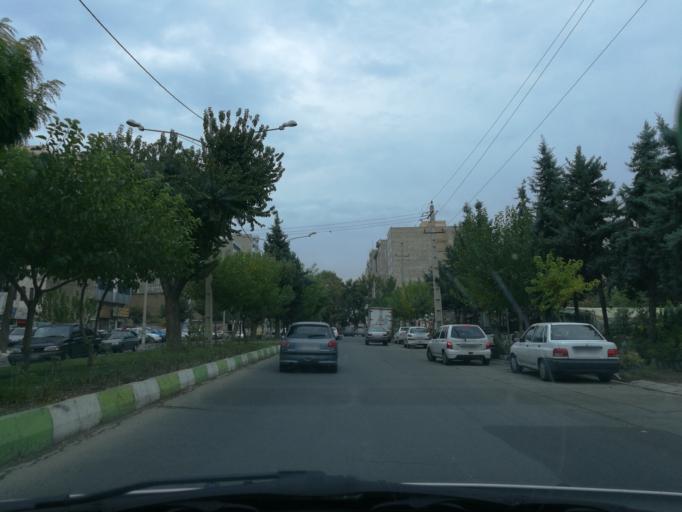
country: IR
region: Alborz
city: Karaj
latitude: 35.8565
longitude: 50.9519
